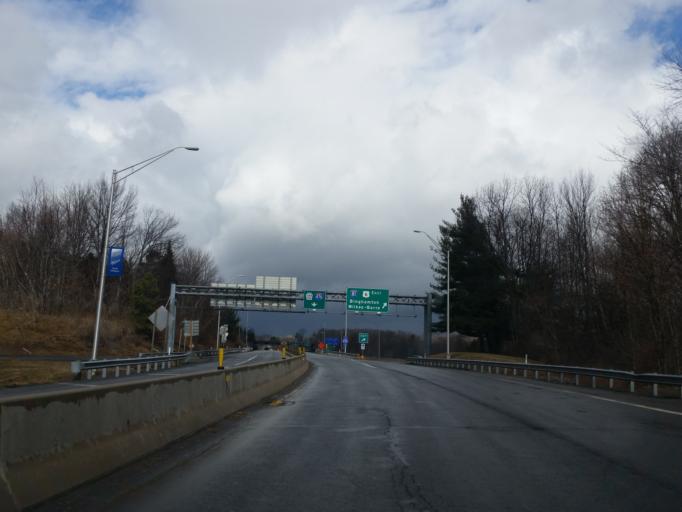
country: US
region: Pennsylvania
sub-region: Lackawanna County
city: Chinchilla
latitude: 41.4810
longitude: -75.6833
